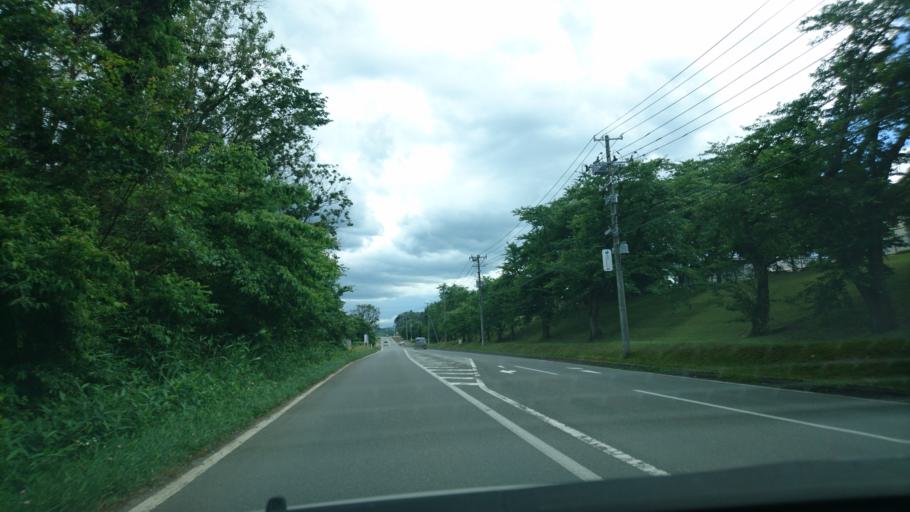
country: JP
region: Iwate
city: Kitakami
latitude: 39.3292
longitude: 141.1278
